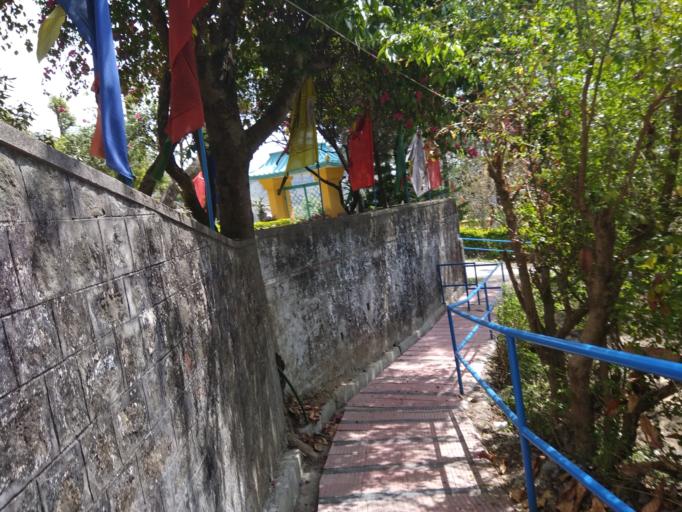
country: IN
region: Himachal Pradesh
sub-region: Kangra
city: Palampur
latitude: 32.0759
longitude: 76.6247
